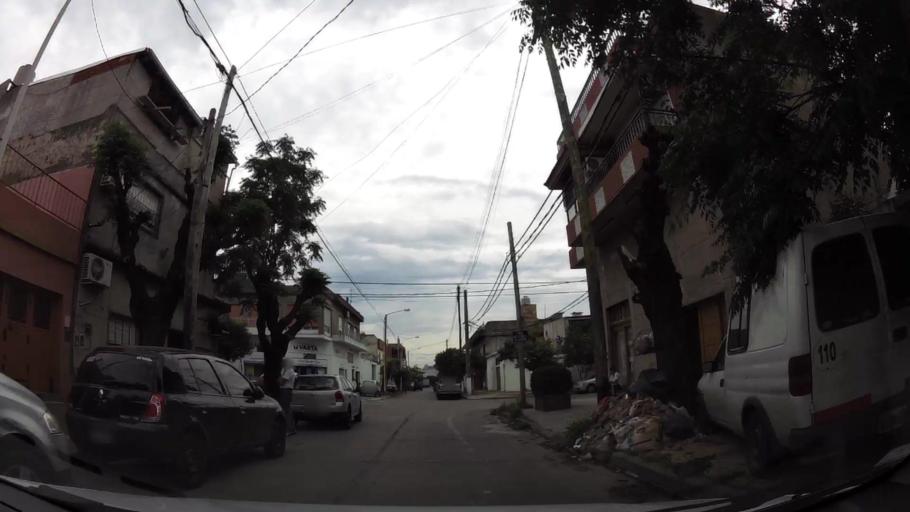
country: AR
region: Buenos Aires F.D.
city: Villa Lugano
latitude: -34.6812
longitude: -58.5062
